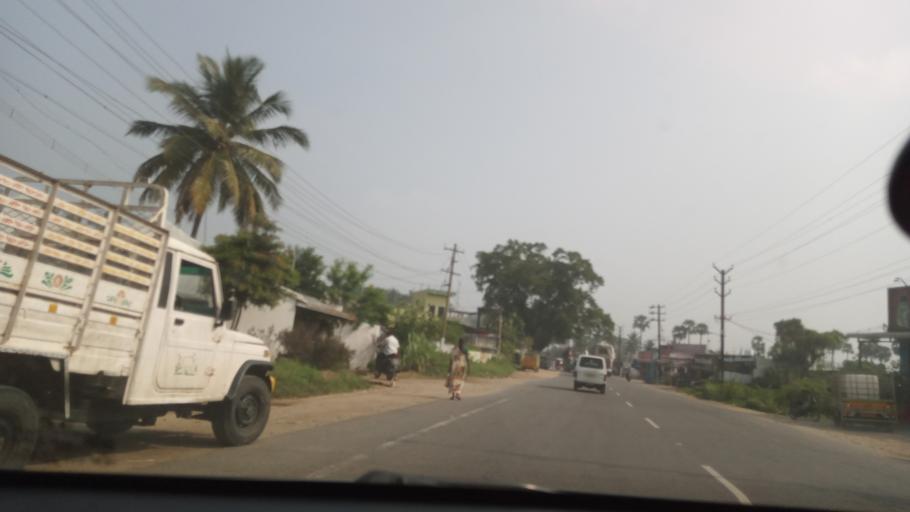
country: IN
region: Tamil Nadu
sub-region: Erode
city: Punjai Puliyampatti
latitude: 11.3449
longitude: 77.1626
